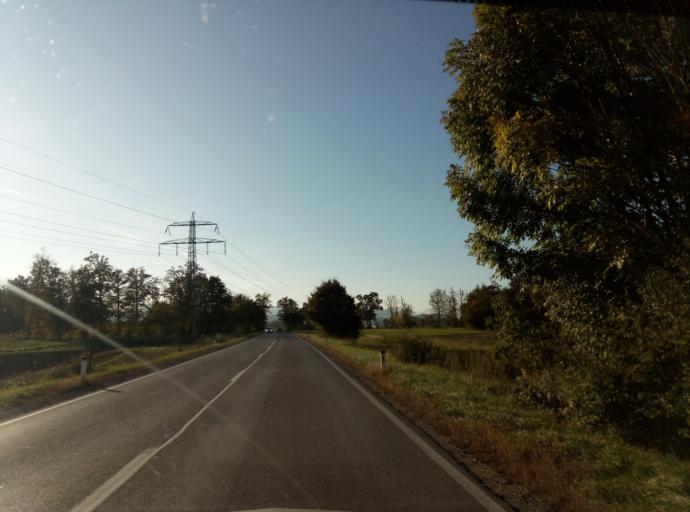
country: SI
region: Ljubljana
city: Ljubljana
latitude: 46.1037
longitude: 14.4972
